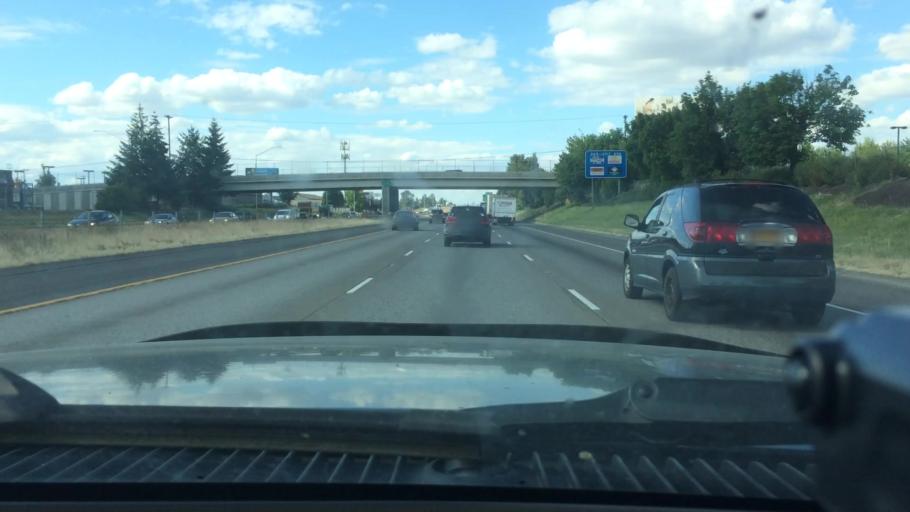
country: US
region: Oregon
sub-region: Marion County
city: Four Corners
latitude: 44.9421
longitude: -122.9902
